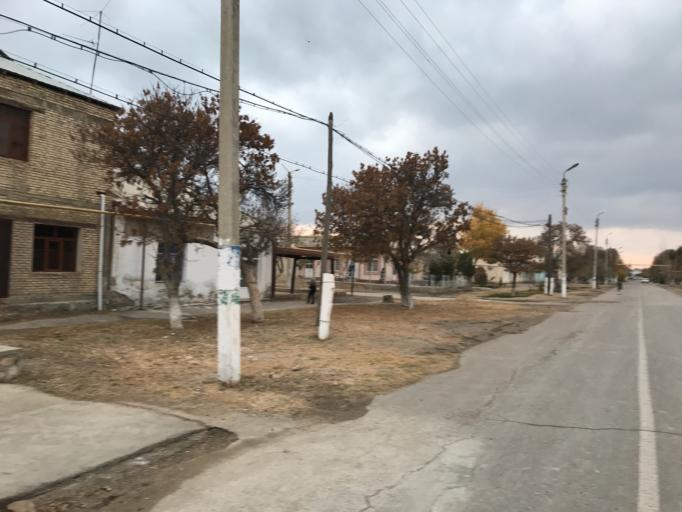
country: UZ
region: Bukhara
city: Kogon
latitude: 39.7169
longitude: 64.5520
